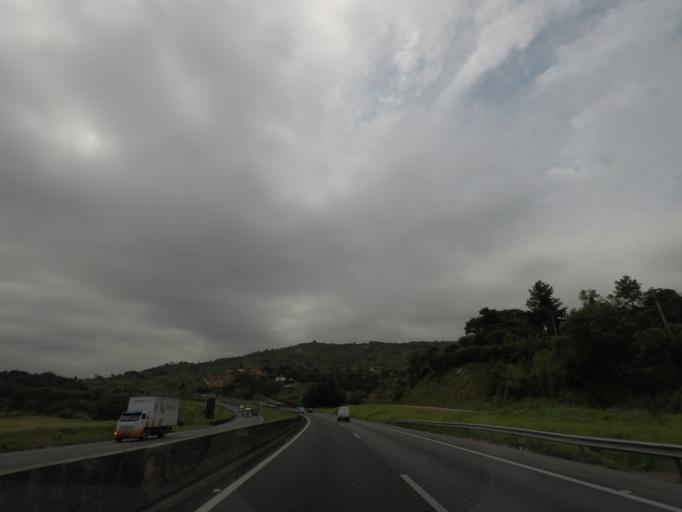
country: BR
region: Sao Paulo
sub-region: Itatiba
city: Itatiba
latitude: -22.9332
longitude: -46.8997
